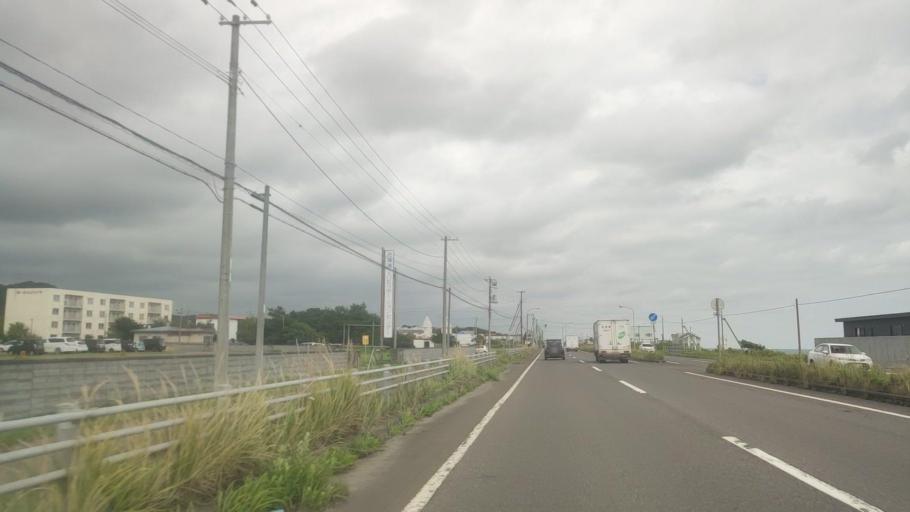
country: JP
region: Hokkaido
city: Shiraoi
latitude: 42.4712
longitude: 141.2315
